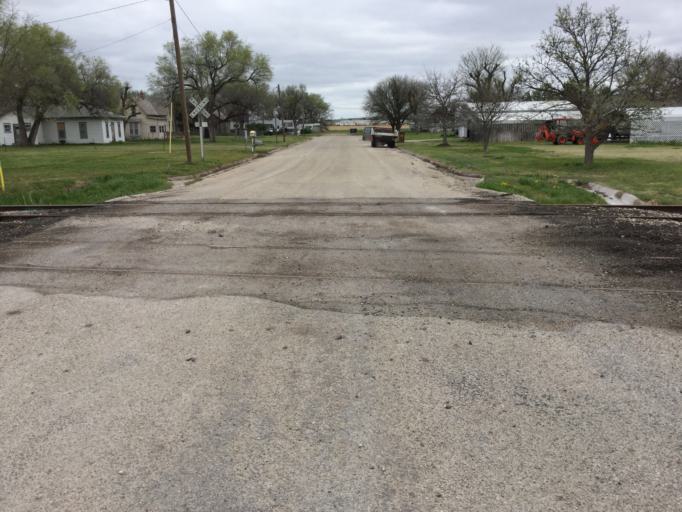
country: US
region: Kansas
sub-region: Osborne County
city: Osborne
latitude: 39.4435
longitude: -98.6985
